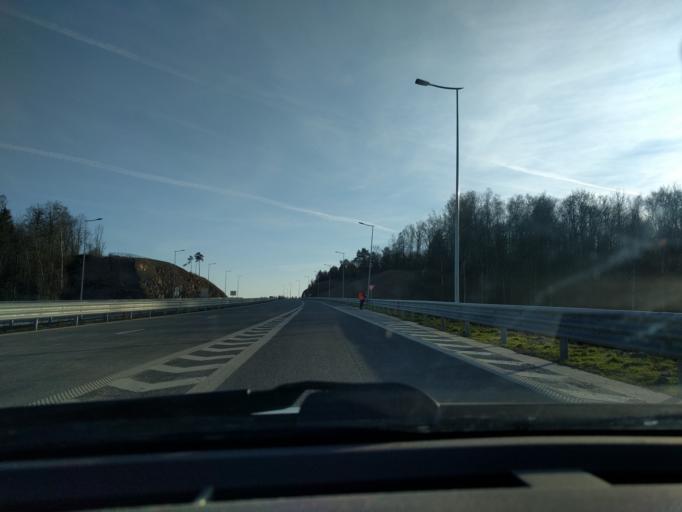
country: BE
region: Wallonia
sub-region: Province de Namur
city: Couvin
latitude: 50.0669
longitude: 4.5047
